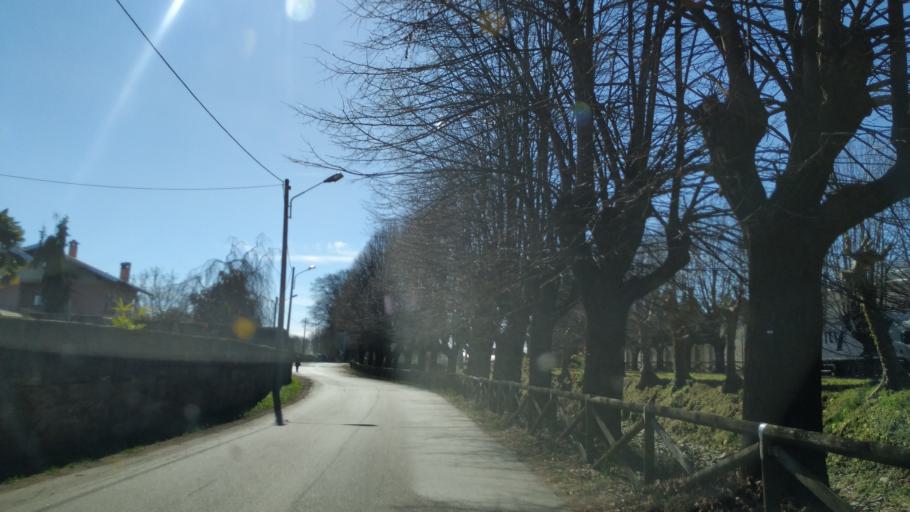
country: IT
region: Piedmont
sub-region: Provincia di Novara
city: Ghemme
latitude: 45.5938
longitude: 8.4220
